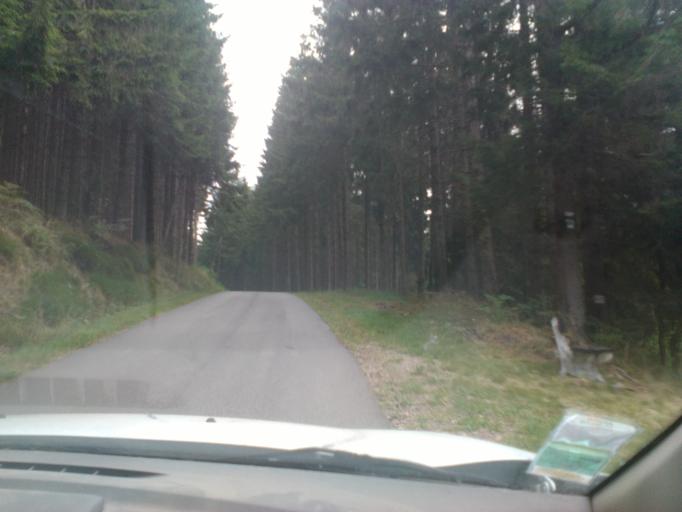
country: FR
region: Lorraine
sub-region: Departement des Vosges
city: Le Tholy
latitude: 48.0962
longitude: 6.7214
